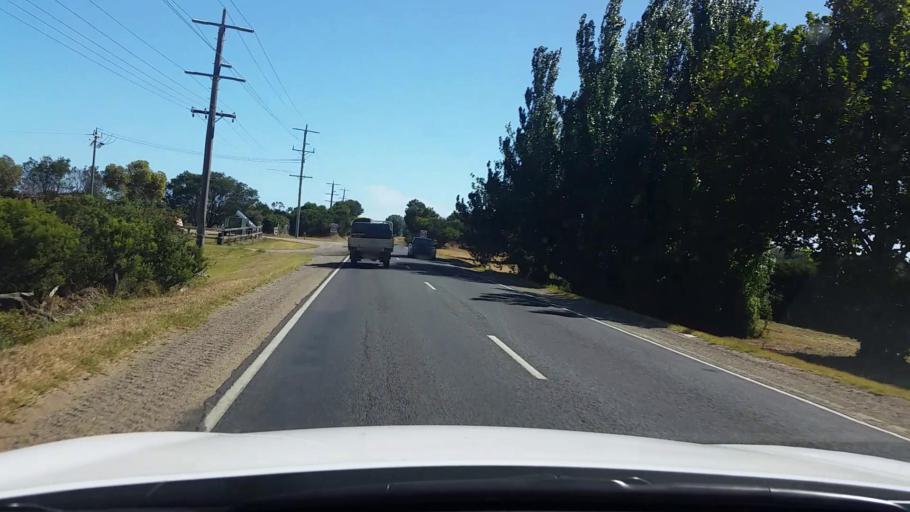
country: AU
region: Victoria
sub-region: Mornington Peninsula
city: Rosebud West
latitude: -38.3909
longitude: 144.8884
